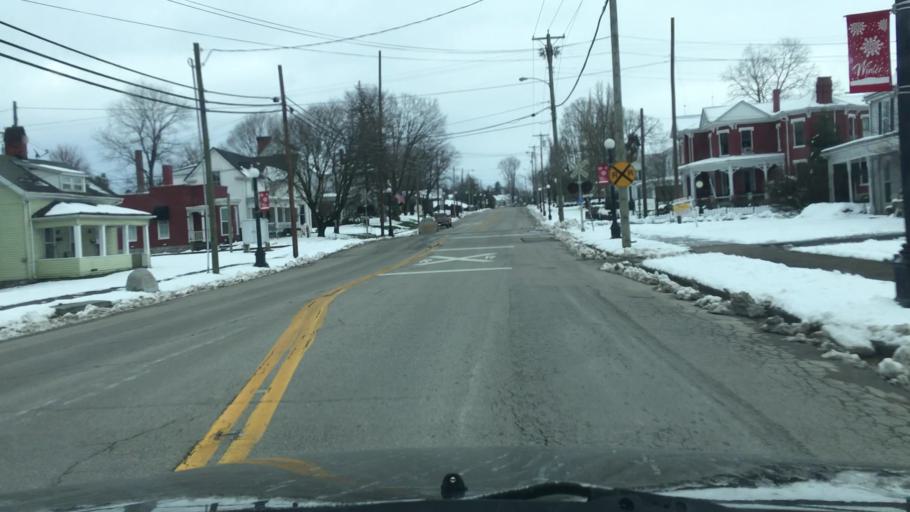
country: US
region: Kentucky
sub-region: Mercer County
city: Harrodsburg
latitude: 37.7622
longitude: -84.8417
